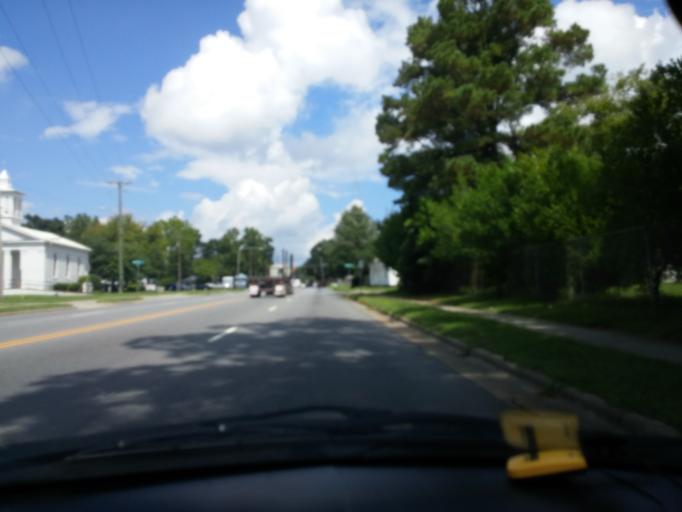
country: US
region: North Carolina
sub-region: Lenoir County
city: Kinston
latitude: 35.2646
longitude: -77.5722
